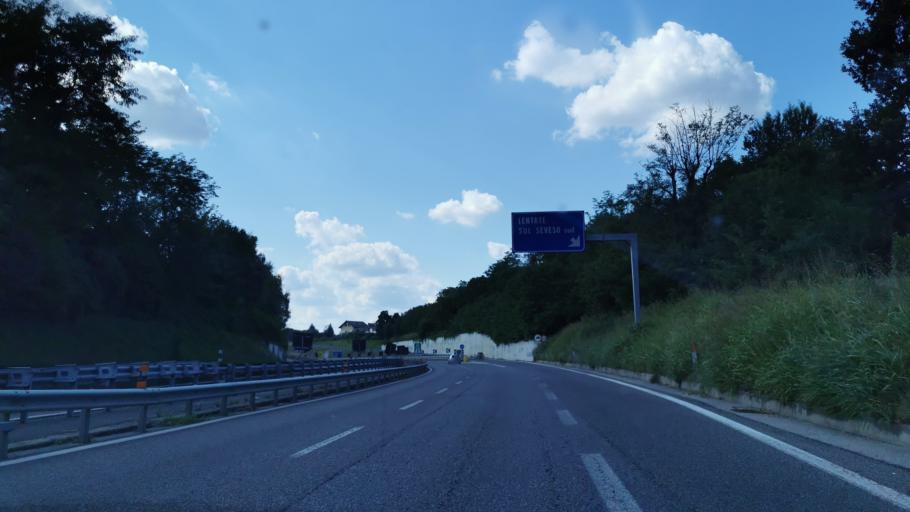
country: IT
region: Lombardy
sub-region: Provincia di Monza e Brianza
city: Barlassina
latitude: 45.6636
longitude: 9.1286
